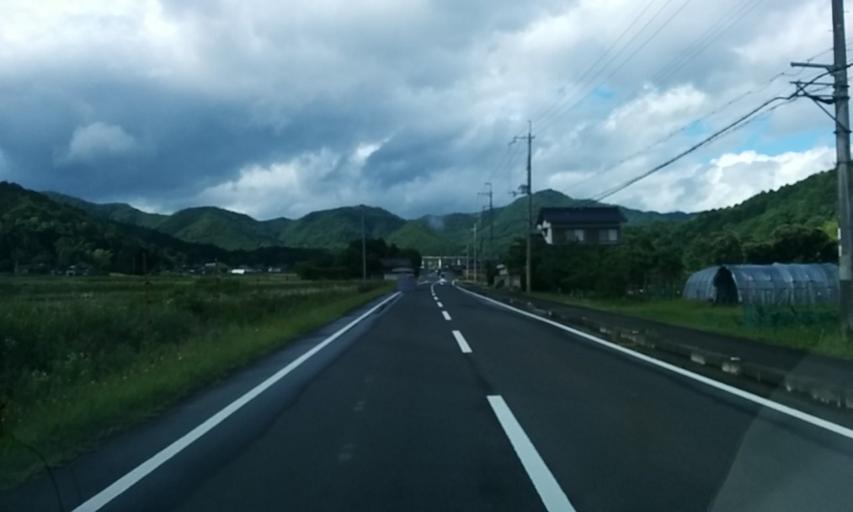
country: JP
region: Kyoto
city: Ayabe
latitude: 35.3764
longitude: 135.2367
